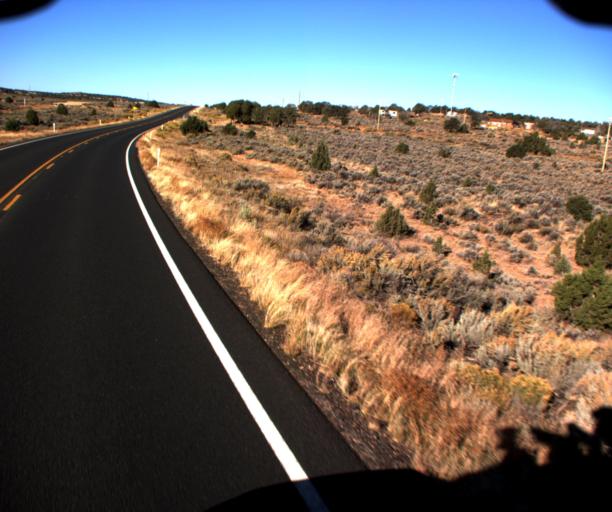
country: US
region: Arizona
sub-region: Apache County
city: Ganado
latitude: 35.7608
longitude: -109.7565
